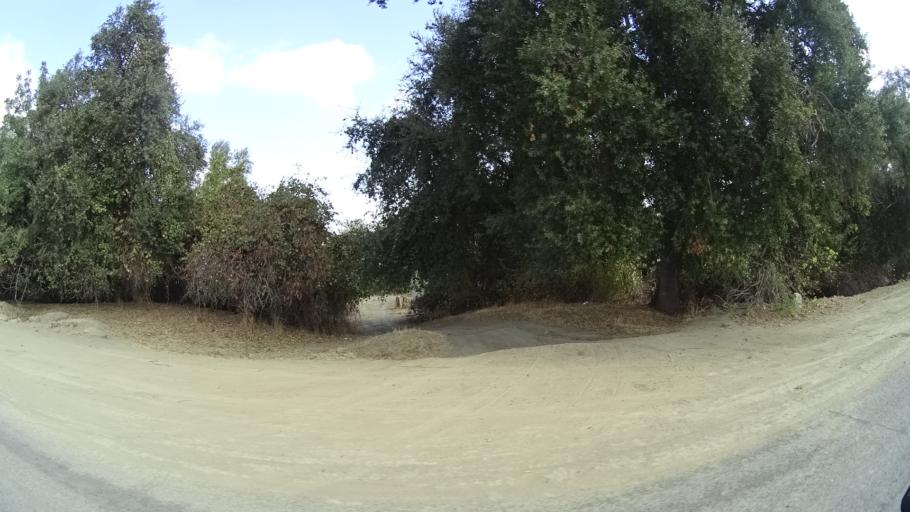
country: US
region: California
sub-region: Yolo County
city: Woodland
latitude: 38.7613
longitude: -121.6799
